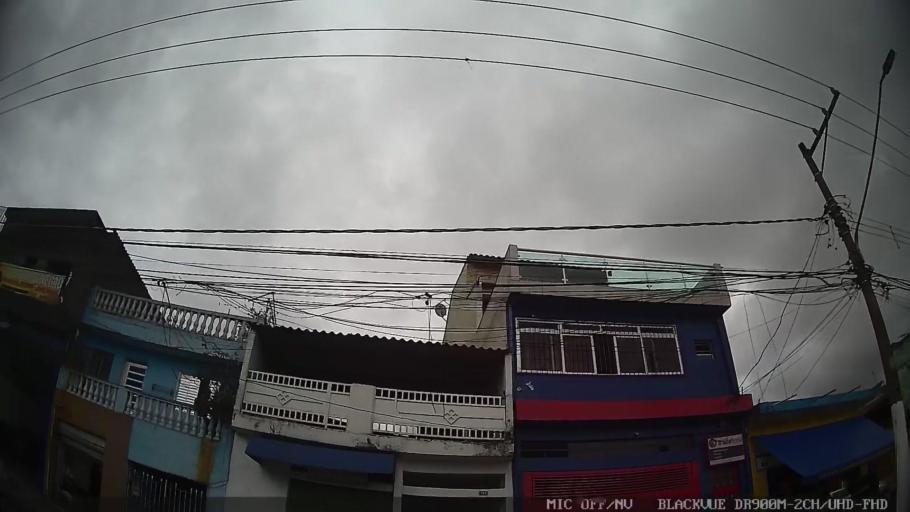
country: BR
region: Sao Paulo
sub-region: Osasco
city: Osasco
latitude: -23.4837
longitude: -46.7089
